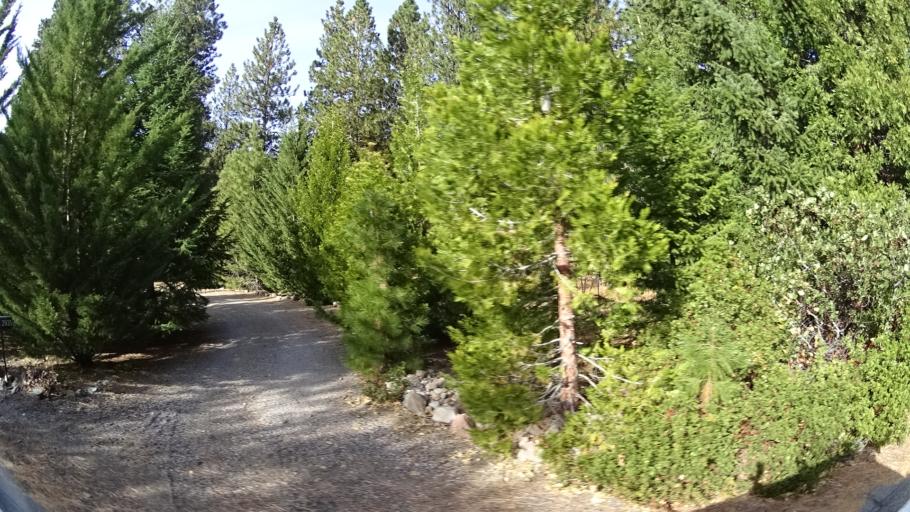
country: US
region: California
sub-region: Siskiyou County
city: Weed
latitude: 41.4045
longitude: -122.4070
